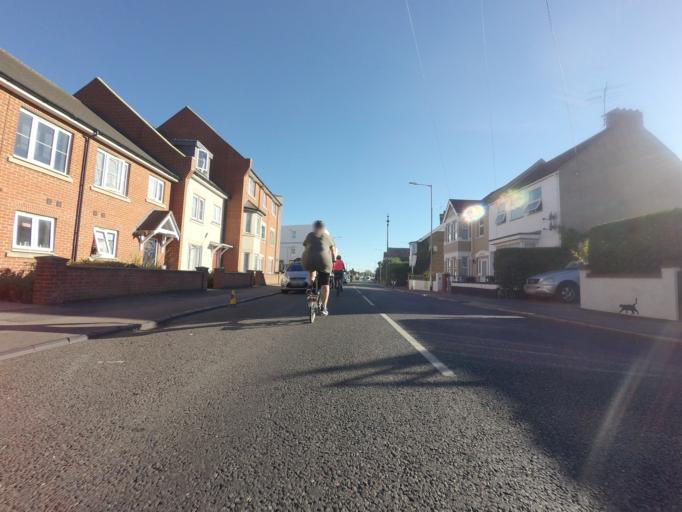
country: GB
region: England
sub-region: Kent
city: Herne Bay
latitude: 51.3689
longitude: 1.1136
